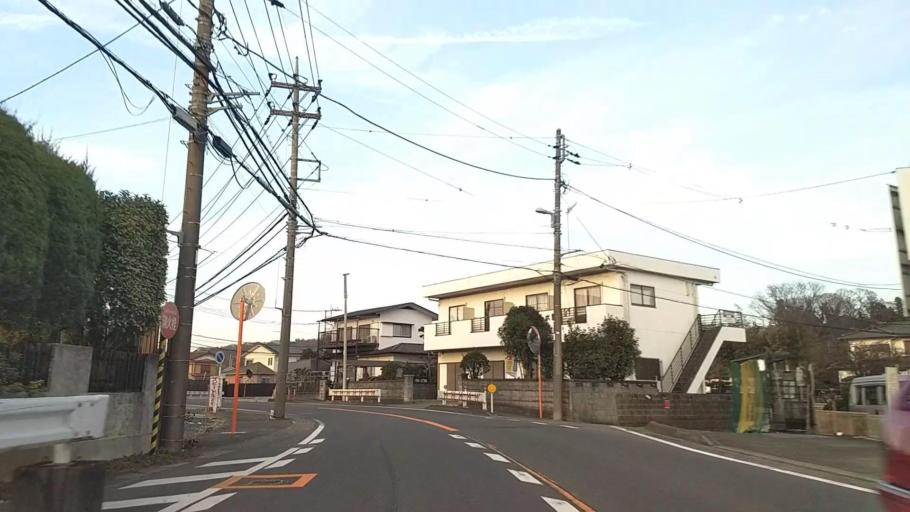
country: JP
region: Kanagawa
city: Atsugi
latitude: 35.4485
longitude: 139.3283
